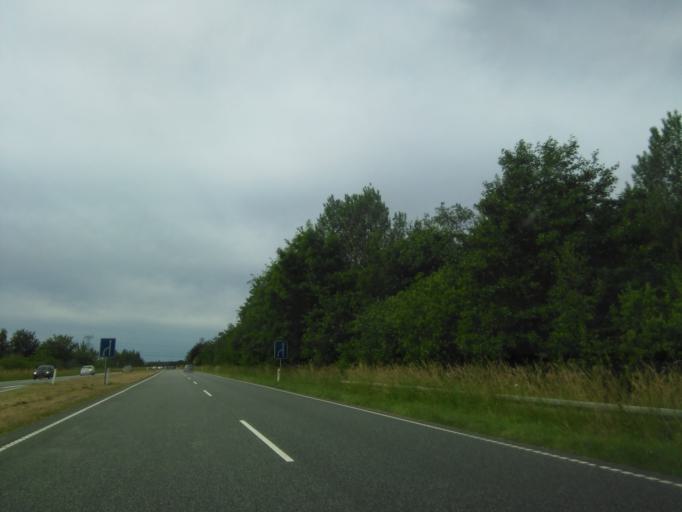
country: DK
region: Central Jutland
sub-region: Arhus Kommune
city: Tranbjerg
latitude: 56.0786
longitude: 10.1121
